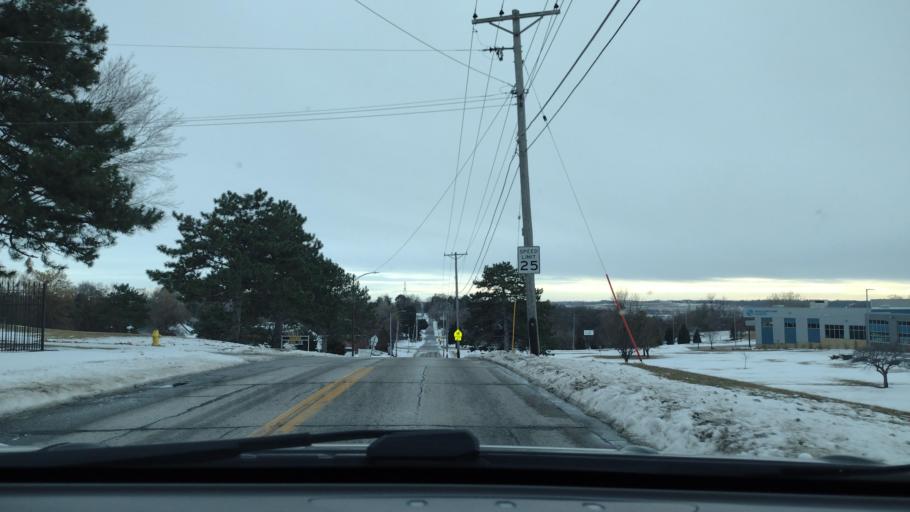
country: US
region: Nebraska
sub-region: Sarpy County
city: La Vista
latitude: 41.1783
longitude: -95.9769
